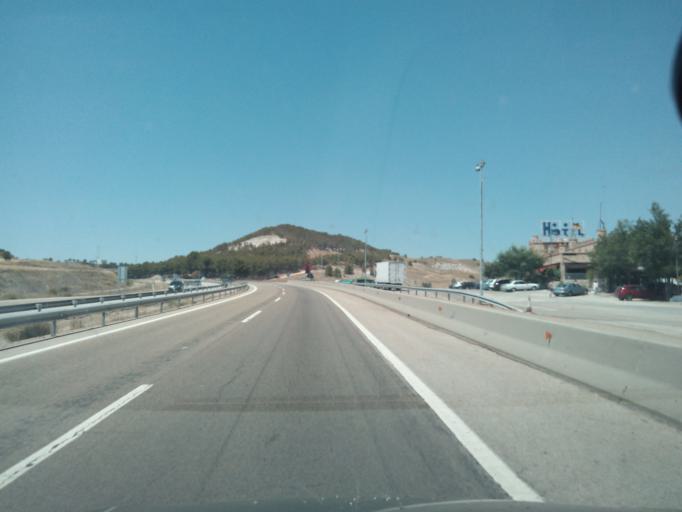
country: ES
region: Castille-La Mancha
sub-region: Province of Toledo
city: Dosbarrios
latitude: 39.8176
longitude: -3.4804
